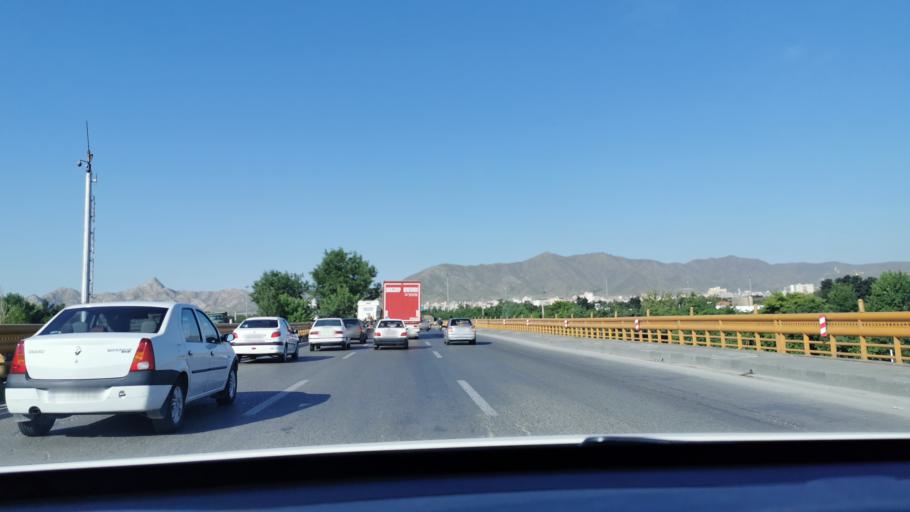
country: IR
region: Razavi Khorasan
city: Mashhad
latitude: 36.2528
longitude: 59.6145
